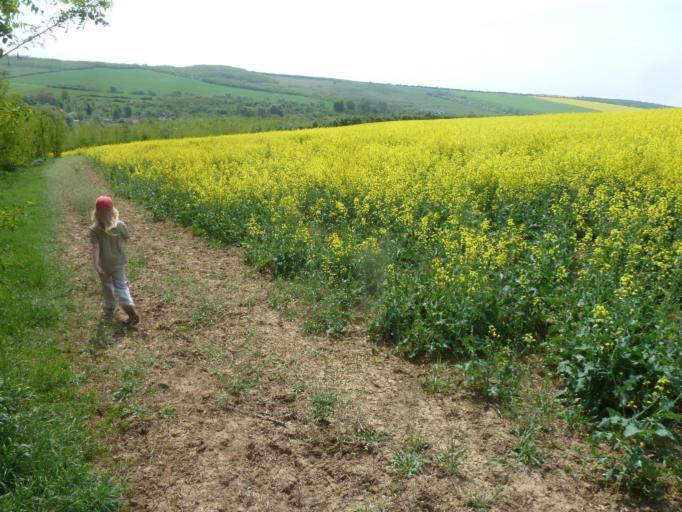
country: HU
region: Borsod-Abauj-Zemplen
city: Halmaj
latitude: 48.3781
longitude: 20.9718
